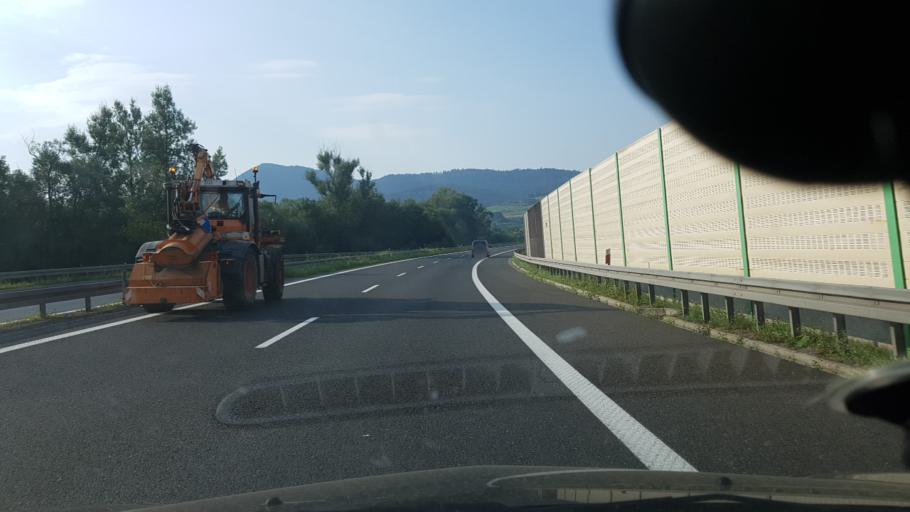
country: PL
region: Lesser Poland Voivodeship
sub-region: Powiat myslenicki
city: Lubien
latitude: 49.7267
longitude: 19.9788
